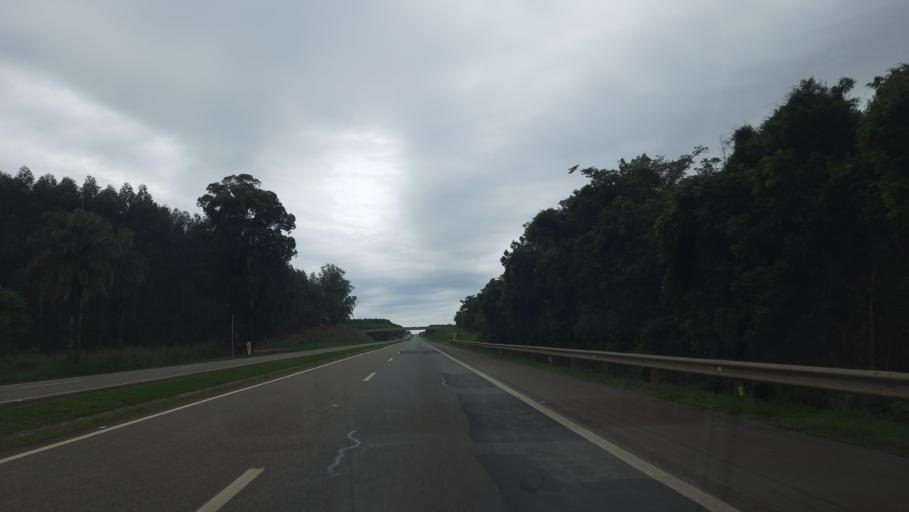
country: BR
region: Sao Paulo
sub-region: Casa Branca
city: Casa Branca
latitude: -21.8538
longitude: -47.0638
